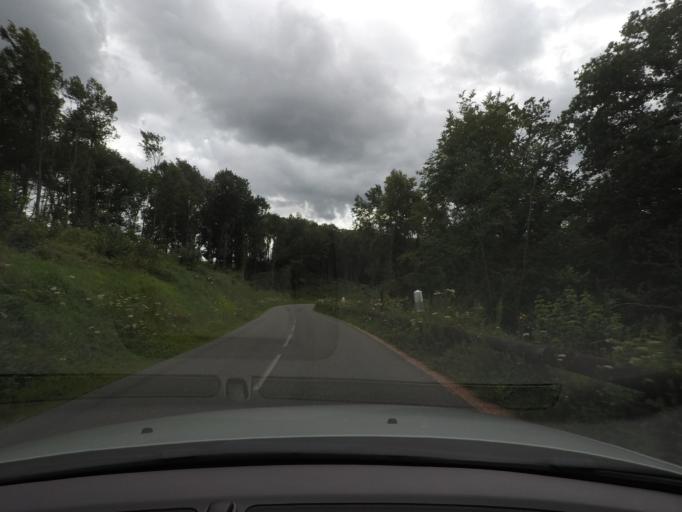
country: FR
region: Haute-Normandie
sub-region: Departement de l'Eure
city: Les Andelys
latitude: 49.2829
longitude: 1.3550
